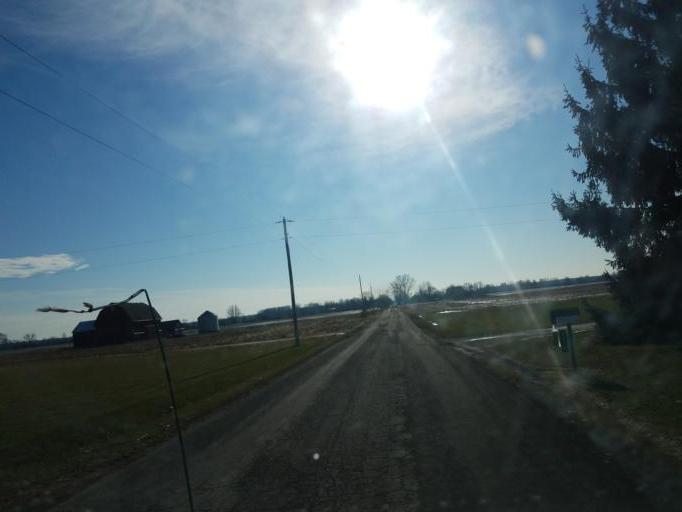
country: US
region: Ohio
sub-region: Morrow County
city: Cardington
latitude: 40.4791
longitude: -82.8694
